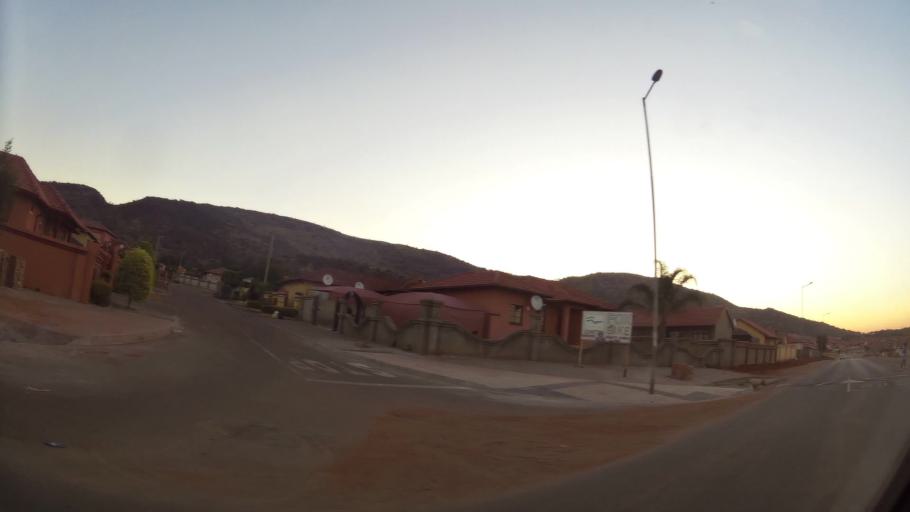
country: ZA
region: North-West
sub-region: Bojanala Platinum District Municipality
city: Rustenburg
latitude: -25.6458
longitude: 27.2009
